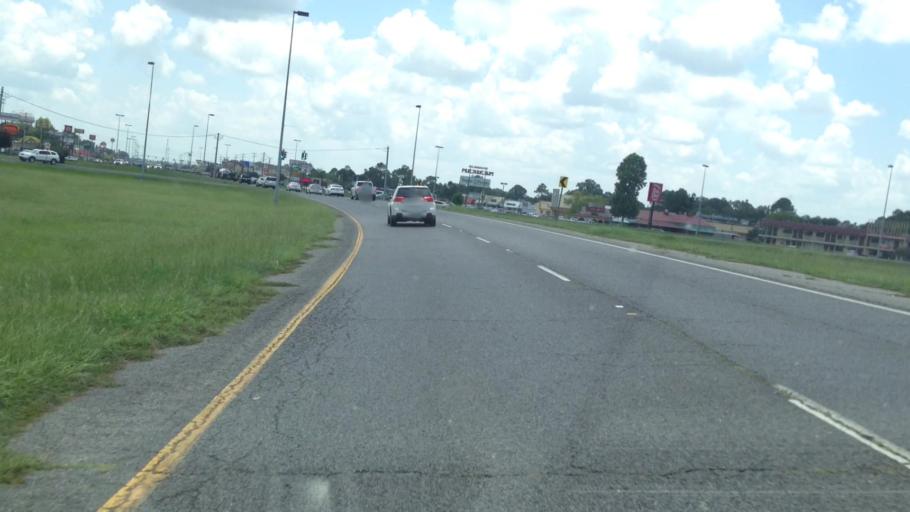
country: US
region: Louisiana
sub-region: Rapides Parish
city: Alexandria
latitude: 31.3001
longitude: -92.4803
